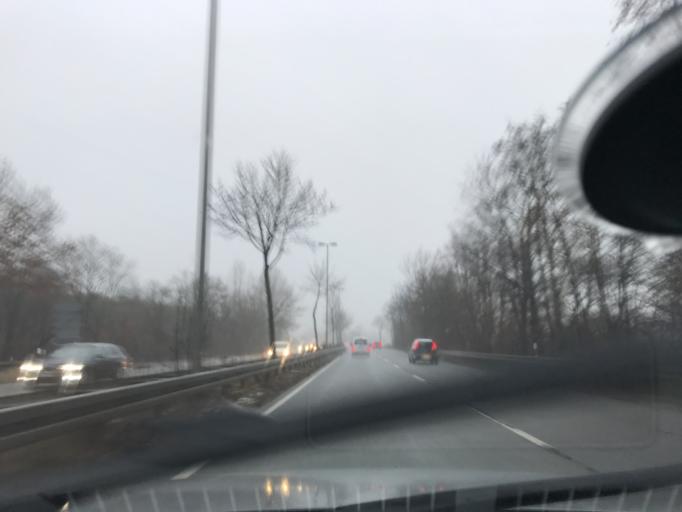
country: DE
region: Lower Saxony
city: Hildesheim
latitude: 52.1728
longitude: 9.9635
